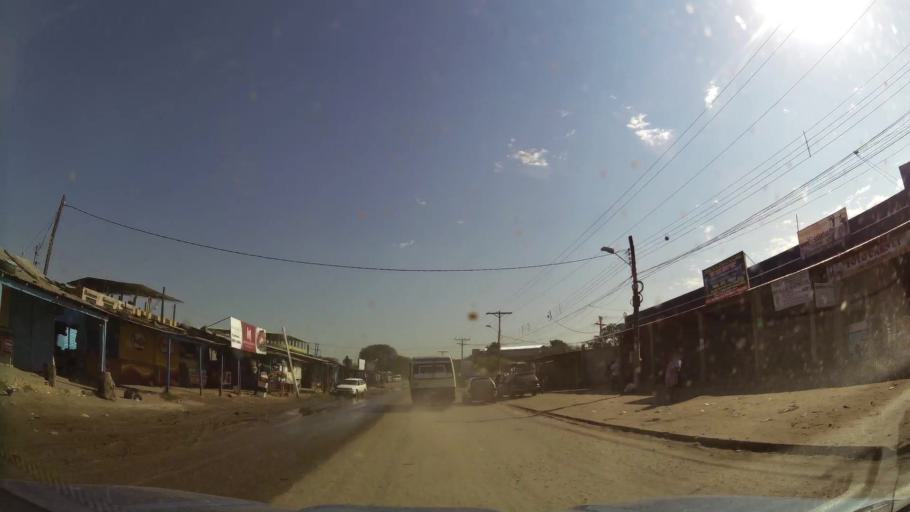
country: BO
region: Santa Cruz
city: Cotoca
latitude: -17.8179
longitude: -63.1179
